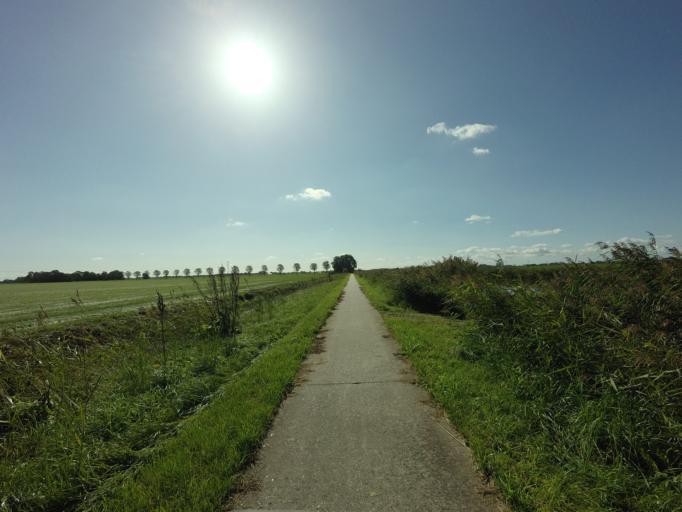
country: NL
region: Friesland
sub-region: Gemeente Boarnsterhim
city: Reduzum
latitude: 53.1227
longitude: 5.7555
